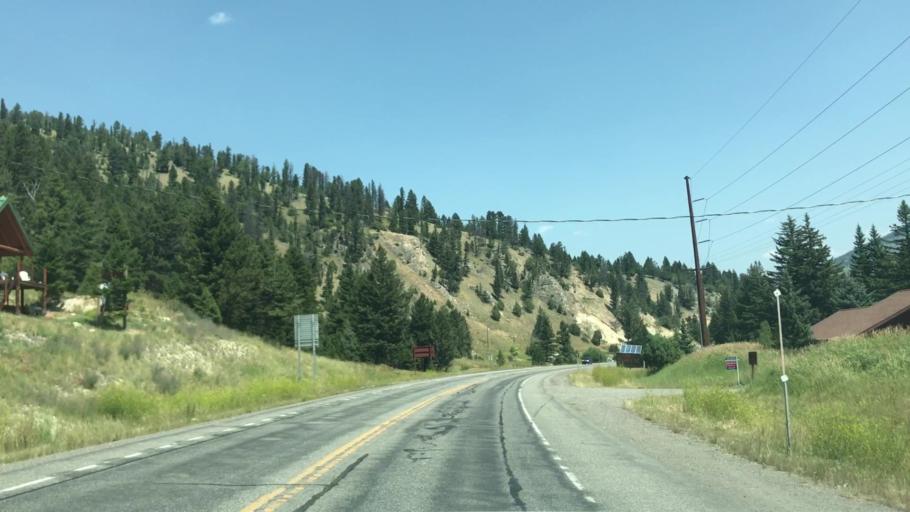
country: US
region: Montana
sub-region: Gallatin County
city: Big Sky
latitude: 45.2673
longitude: -111.2519
